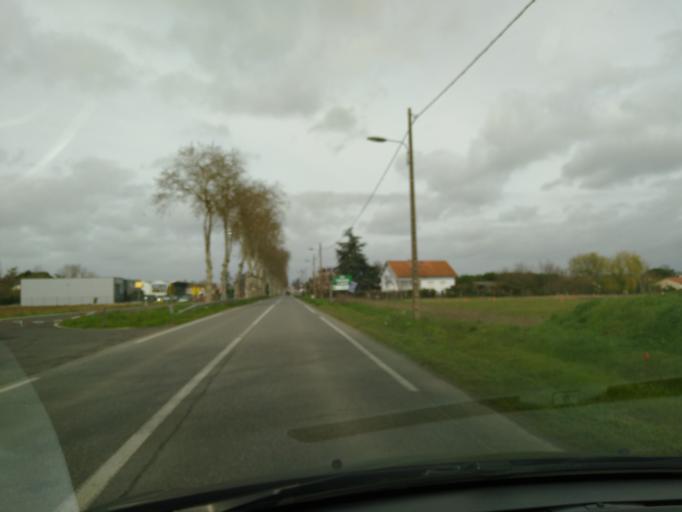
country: FR
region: Midi-Pyrenees
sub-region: Departement de la Haute-Garonne
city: Grenade
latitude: 43.7575
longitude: 1.3017
